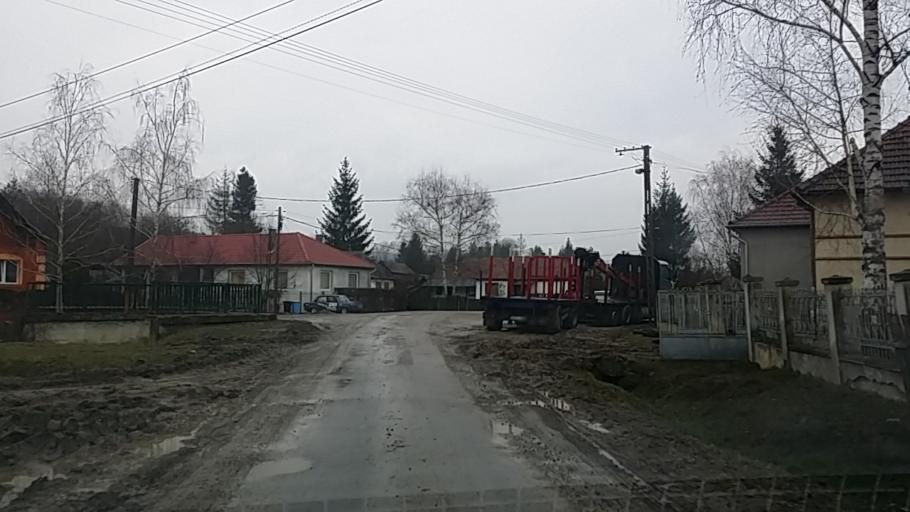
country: HU
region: Borsod-Abauj-Zemplen
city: Rudabanya
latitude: 48.4187
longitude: 20.5551
